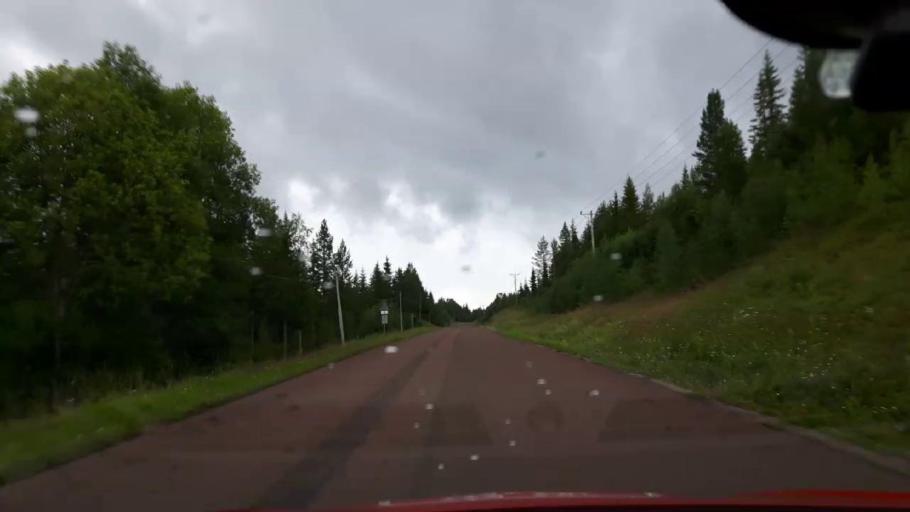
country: SE
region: Jaemtland
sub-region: Are Kommun
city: Jarpen
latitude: 63.3269
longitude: 13.6933
